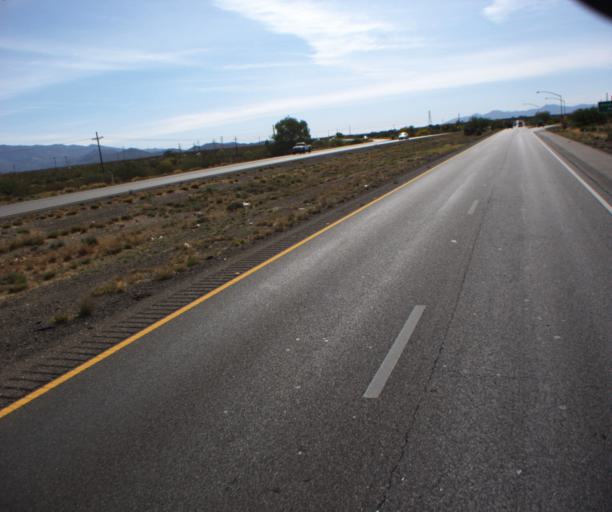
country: US
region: Arizona
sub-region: Pima County
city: Vail
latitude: 32.0645
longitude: -110.7786
